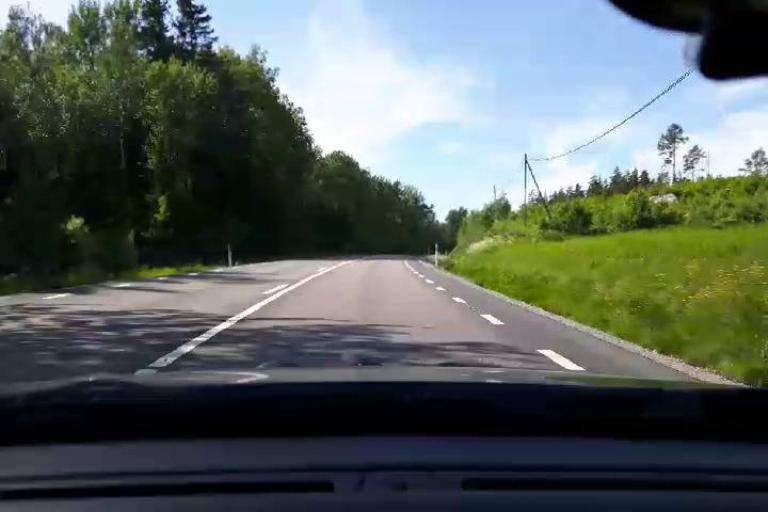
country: SE
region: Gaevleborg
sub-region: Bollnas Kommun
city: Kilafors
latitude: 61.1729
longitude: 16.8000
